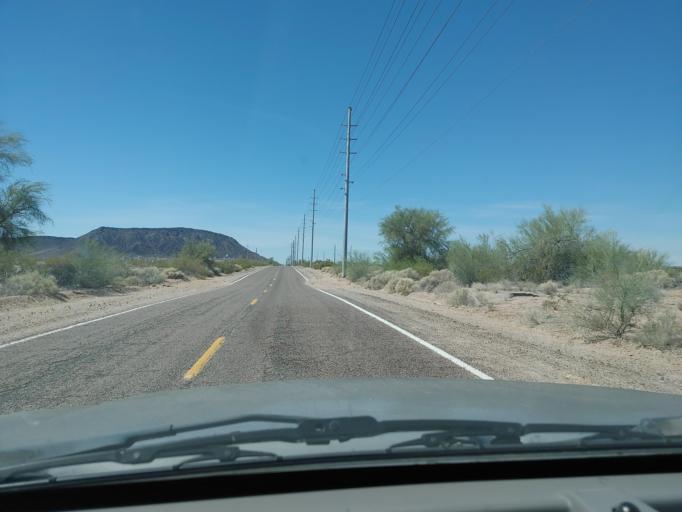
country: US
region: Arizona
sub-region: Maricopa County
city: Gila Bend
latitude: 33.0279
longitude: -113.3245
